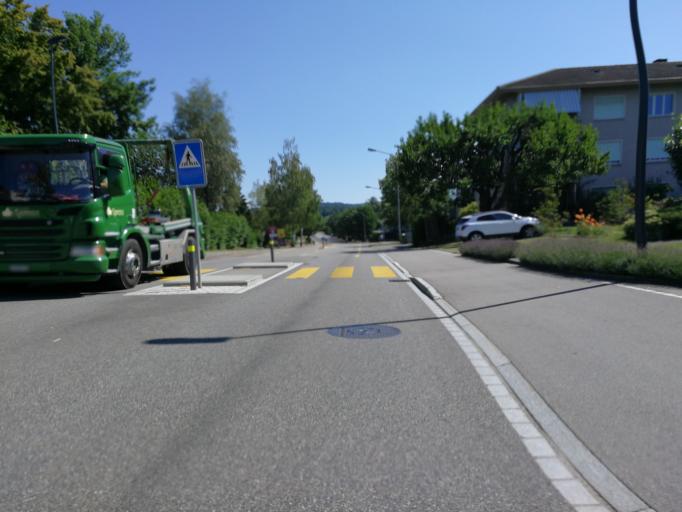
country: CH
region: Zurich
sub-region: Bezirk Uster
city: Uster / Nieder-Uster
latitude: 47.3499
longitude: 8.7019
